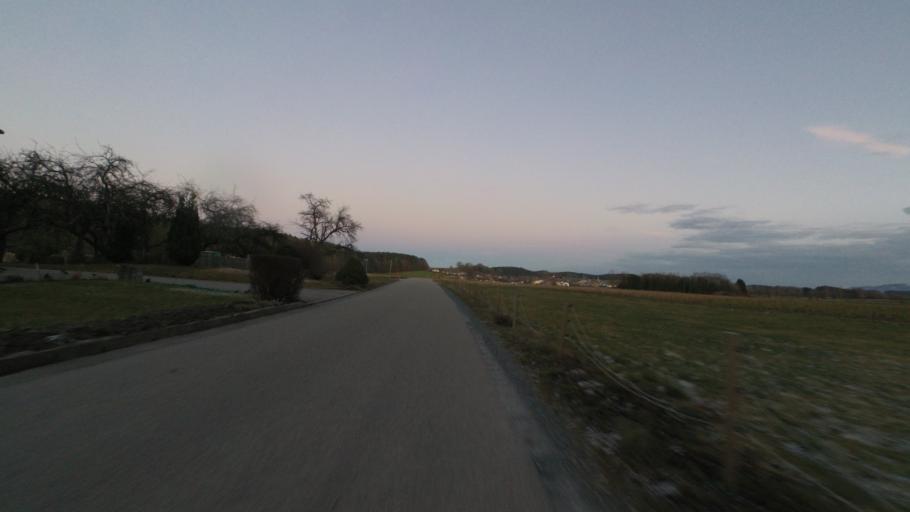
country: DE
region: Bavaria
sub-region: Upper Bavaria
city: Chieming
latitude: 47.9100
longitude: 12.5455
